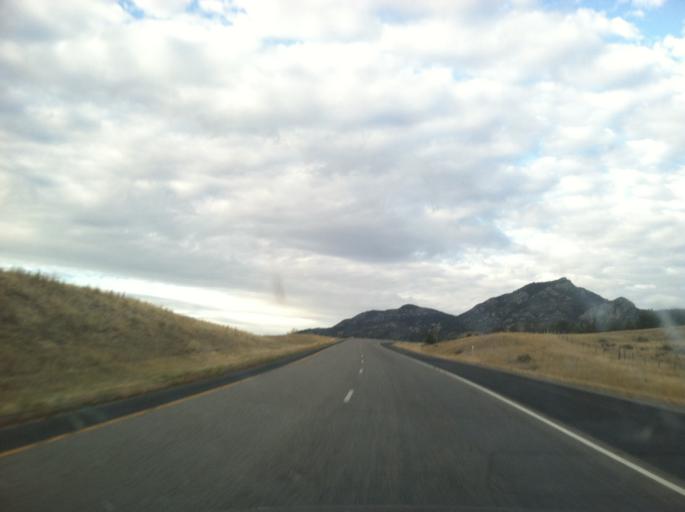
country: US
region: Montana
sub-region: Jefferson County
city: Whitehall
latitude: 45.8764
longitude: -111.9260
